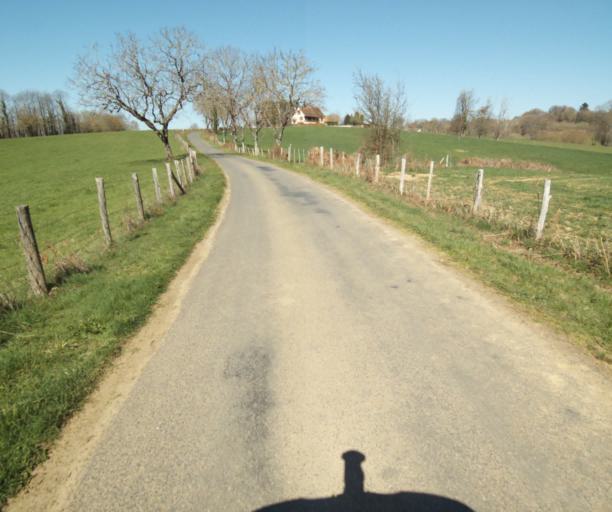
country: FR
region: Limousin
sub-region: Departement de la Correze
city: Saint-Clement
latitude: 45.3320
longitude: 1.7084
